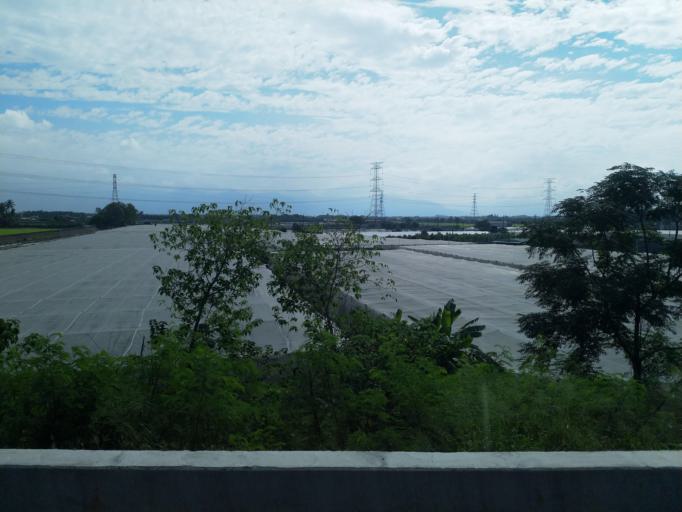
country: TW
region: Taiwan
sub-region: Pingtung
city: Pingtung
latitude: 22.8276
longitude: 120.4891
